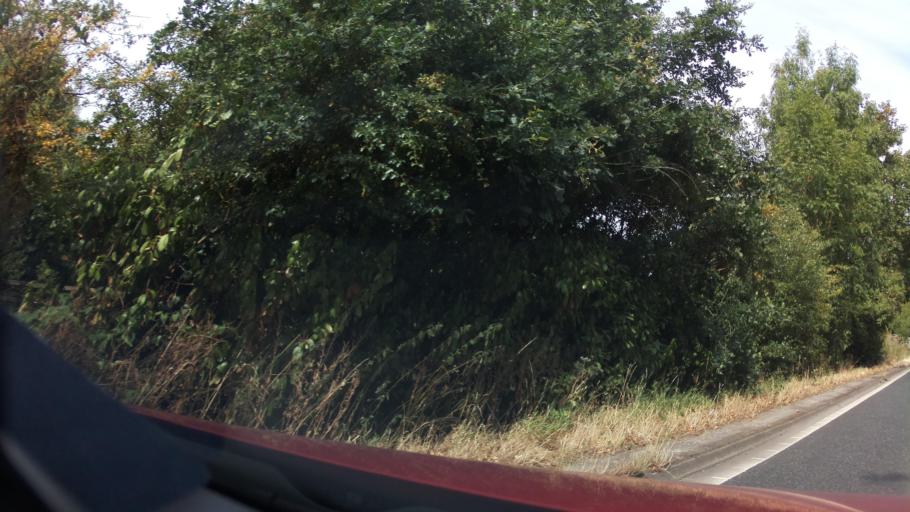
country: GB
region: England
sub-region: Surrey
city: Salfords
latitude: 51.2067
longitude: -0.1988
